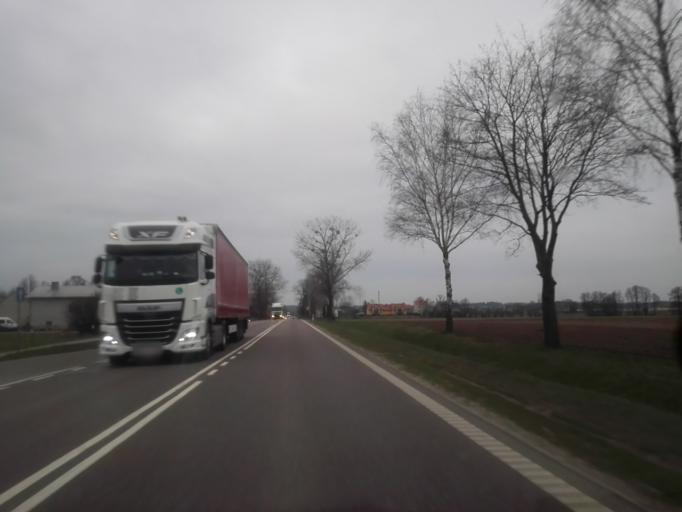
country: PL
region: Podlasie
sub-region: Powiat grajewski
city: Szczuczyn
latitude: 53.5707
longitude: 22.2932
